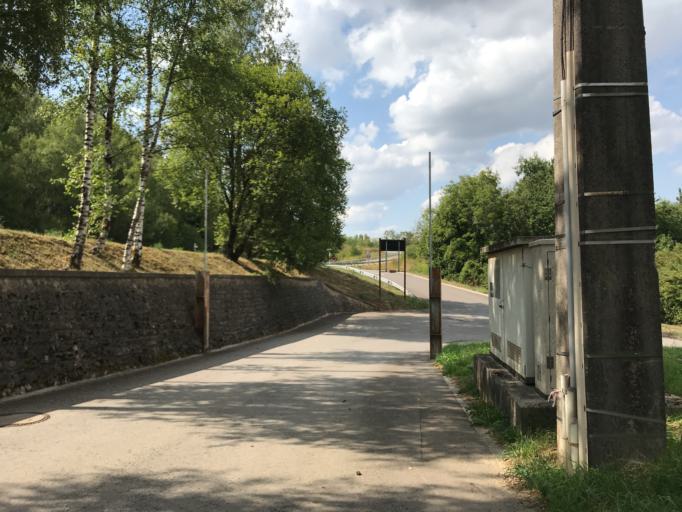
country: FR
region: Lorraine
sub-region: Departement de Meurthe-et-Moselle
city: Thil
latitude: 49.4918
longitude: 5.9123
